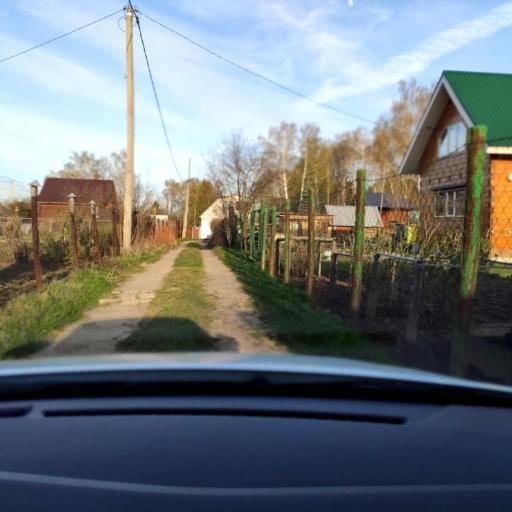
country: RU
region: Tatarstan
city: Stolbishchi
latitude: 55.6010
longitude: 49.0988
